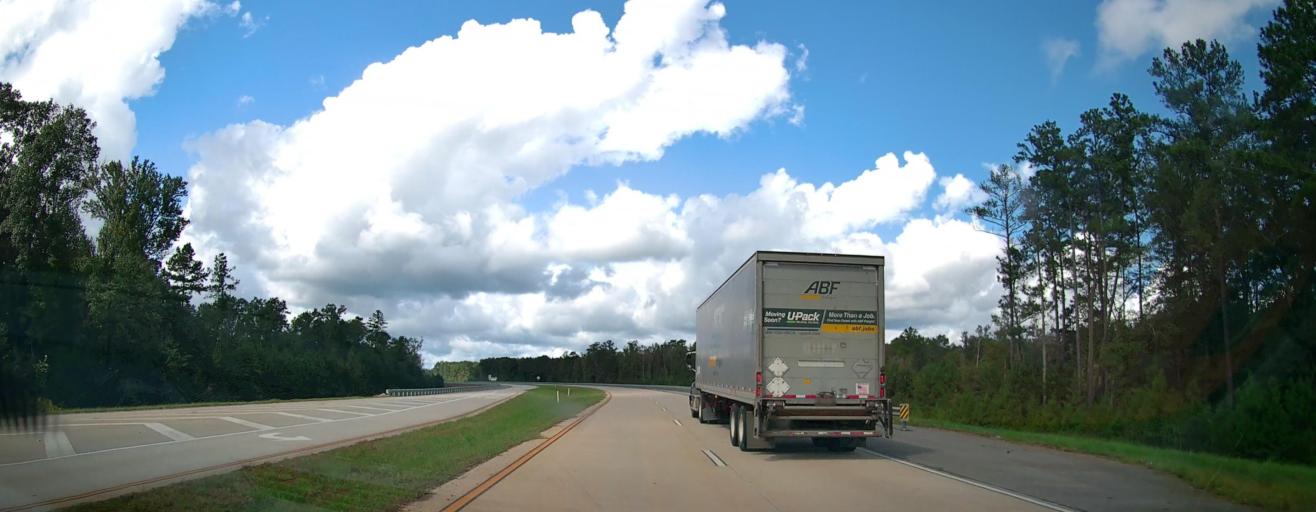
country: US
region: Georgia
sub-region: Jones County
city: Gray
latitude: 33.0179
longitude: -83.5129
